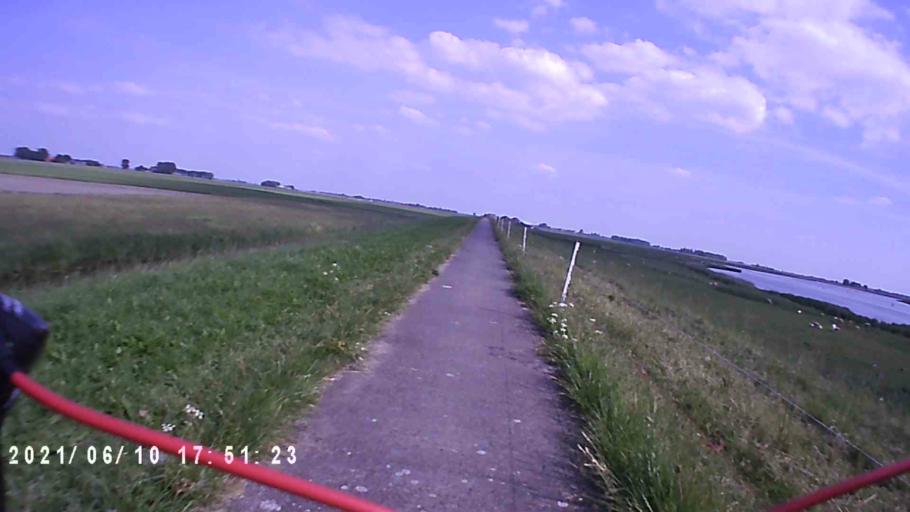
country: NL
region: Groningen
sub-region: Gemeente De Marne
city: Ulrum
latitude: 53.3306
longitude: 6.3140
